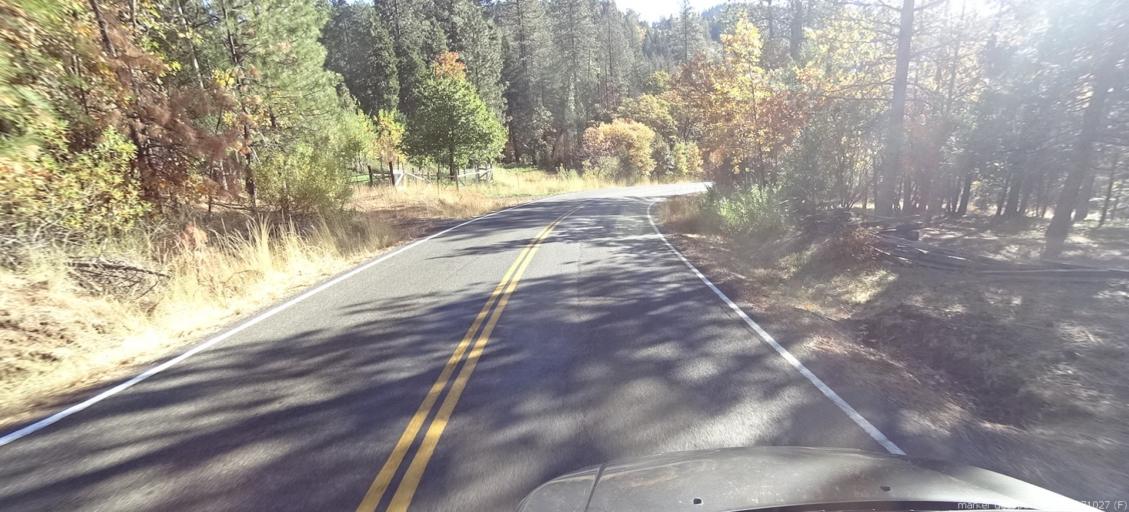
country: US
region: California
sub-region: Shasta County
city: Burney
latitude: 40.9143
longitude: -121.9096
